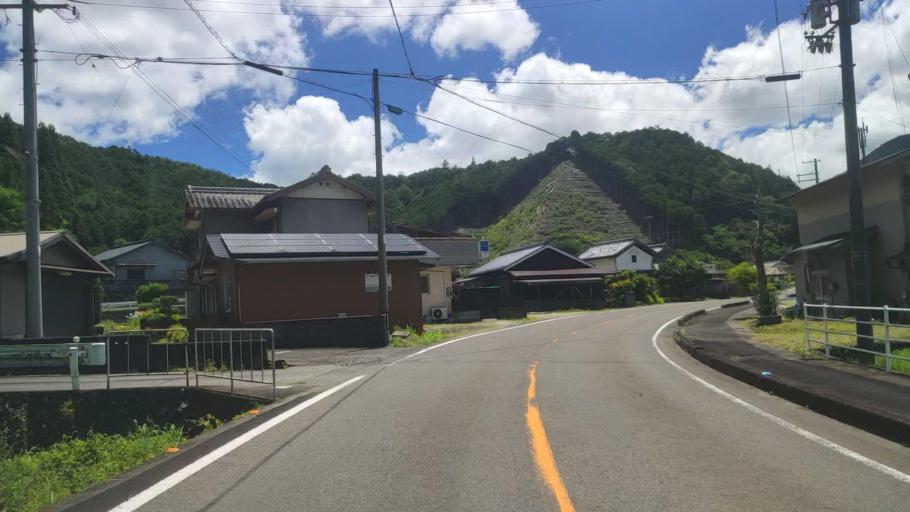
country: JP
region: Mie
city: Owase
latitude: 33.9857
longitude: 136.0482
